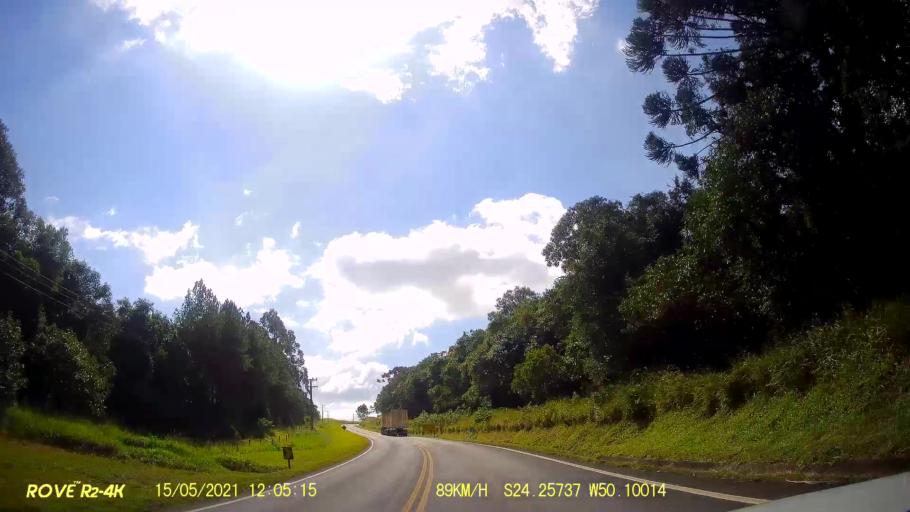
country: BR
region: Parana
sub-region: Pirai Do Sul
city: Pirai do Sul
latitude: -24.2572
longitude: -50.1002
